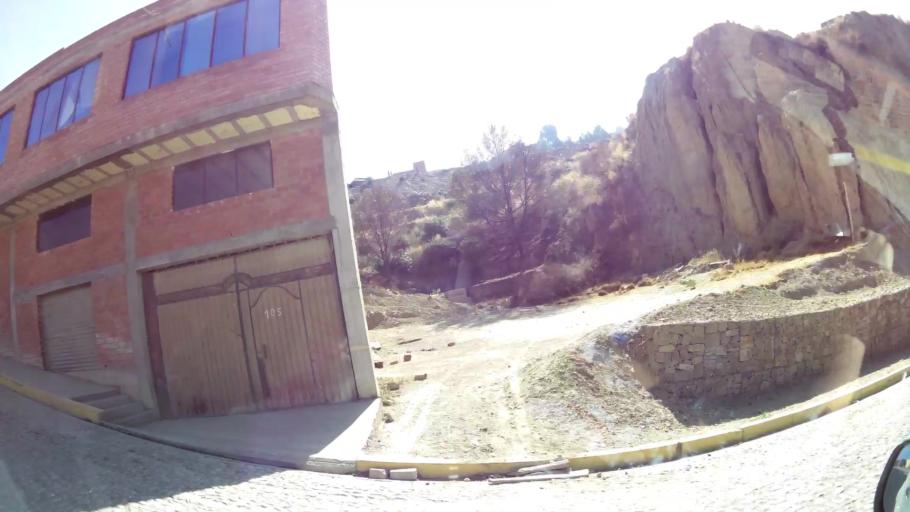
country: BO
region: La Paz
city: La Paz
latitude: -16.5055
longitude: -68.1101
